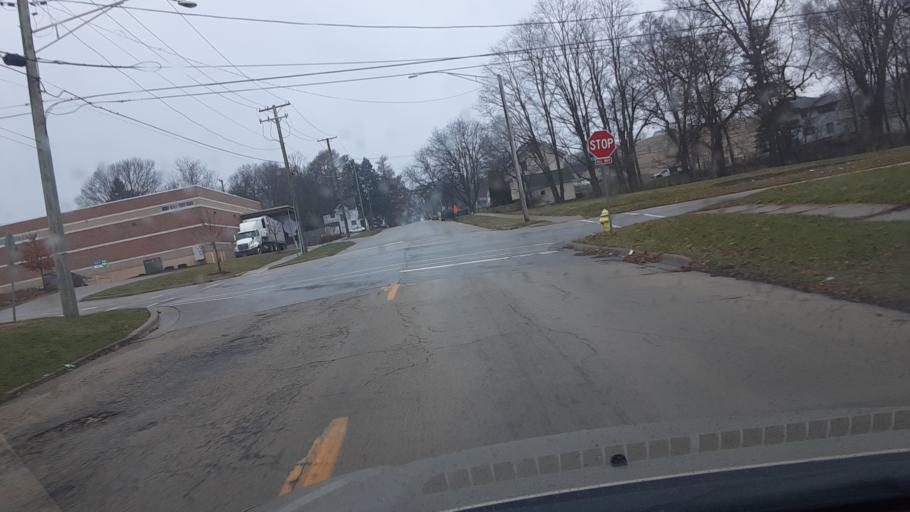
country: US
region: Illinois
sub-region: Winnebago County
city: Rockford
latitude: 42.2773
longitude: -89.1157
